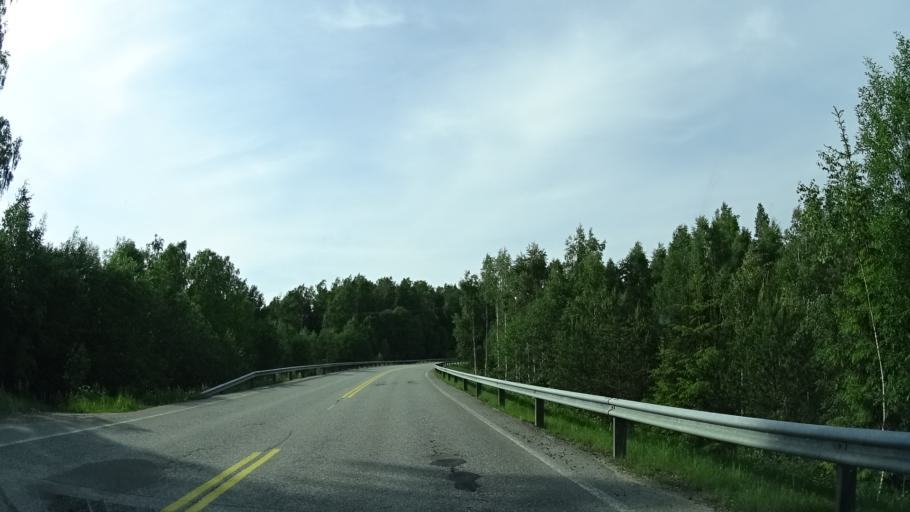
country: FI
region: Uusimaa
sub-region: Helsinki
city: Kirkkonummi
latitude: 60.1126
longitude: 24.4830
